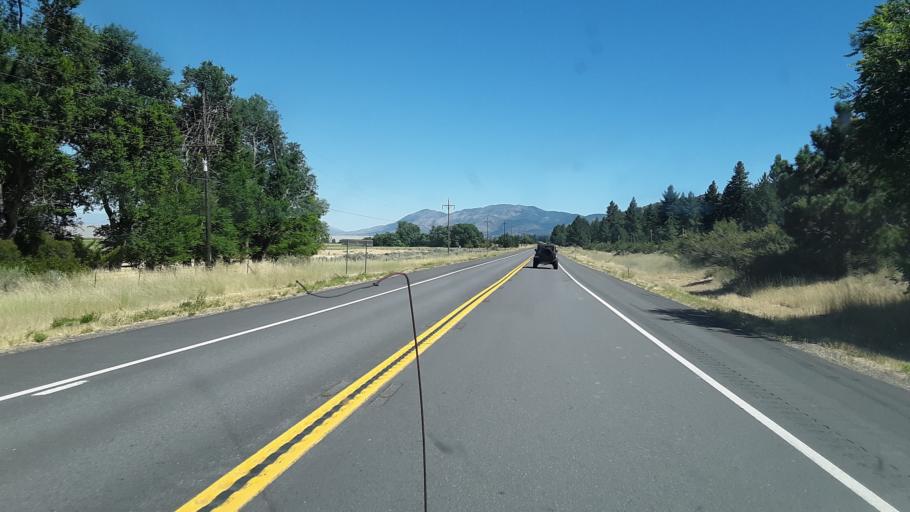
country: US
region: California
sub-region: Lassen County
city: Janesville
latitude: 40.2456
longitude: -120.4572
